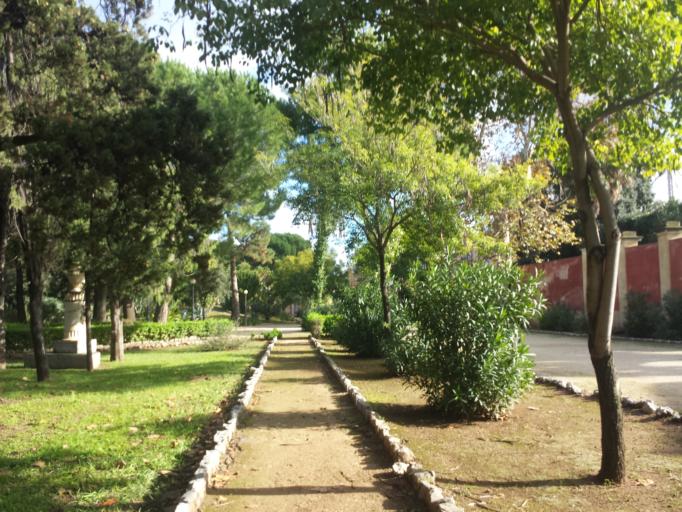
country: IT
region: Sicily
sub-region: Palermo
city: Palermo
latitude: 38.1124
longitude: 13.3758
